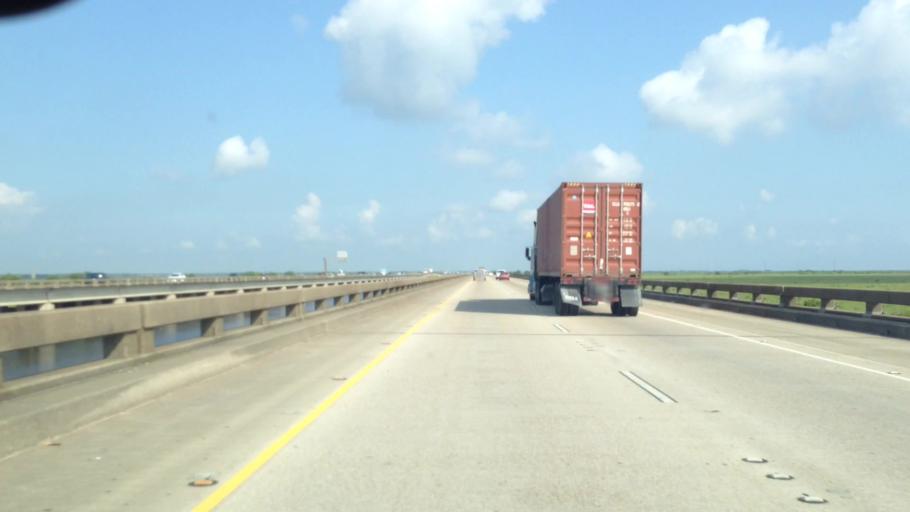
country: US
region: Louisiana
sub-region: Saint Charles Parish
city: Ama
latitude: 30.0223
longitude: -90.3223
